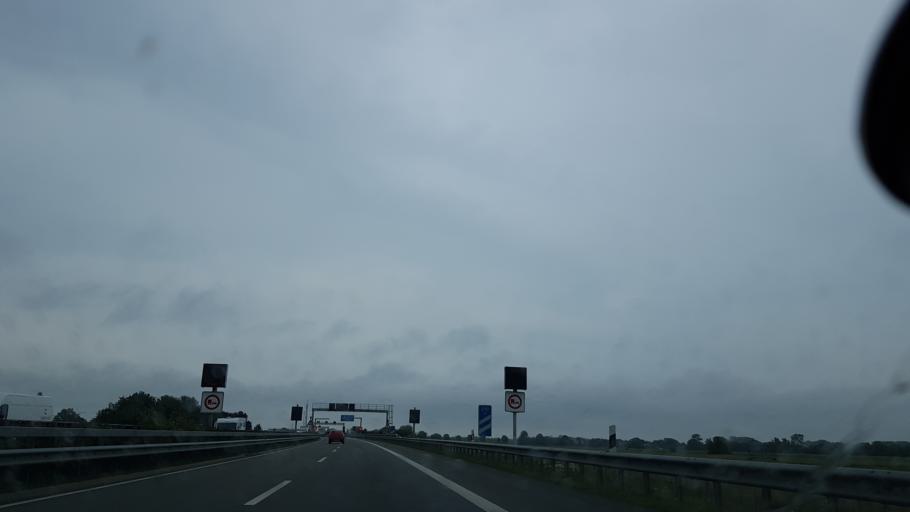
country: DE
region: Lower Saxony
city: Jemgum
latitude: 53.2254
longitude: 7.3879
